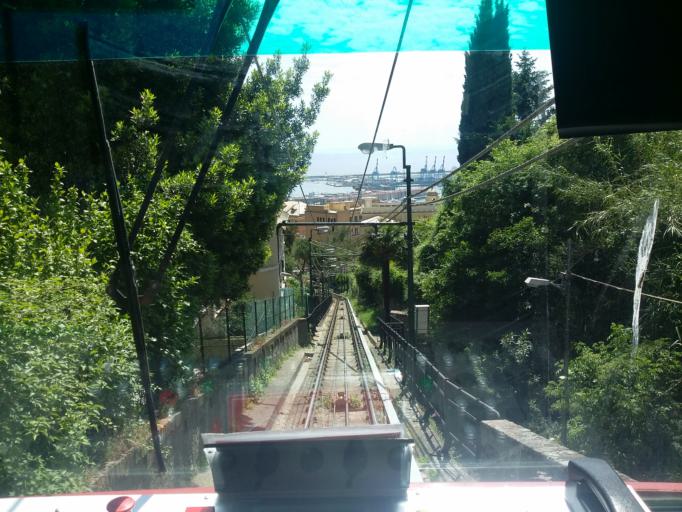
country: IT
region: Liguria
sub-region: Provincia di Genova
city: Genoa
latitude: 44.4212
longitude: 8.9327
